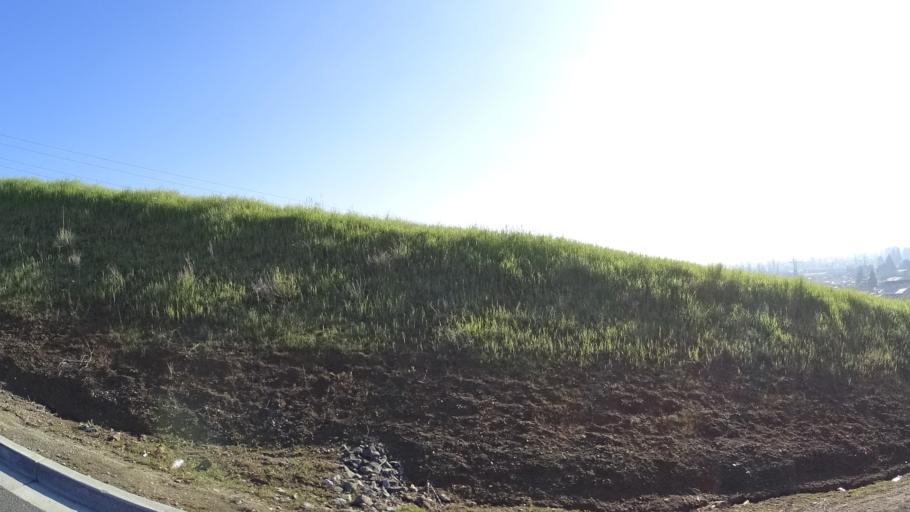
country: US
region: California
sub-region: Alameda County
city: Hayward
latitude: 37.6612
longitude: -122.0707
